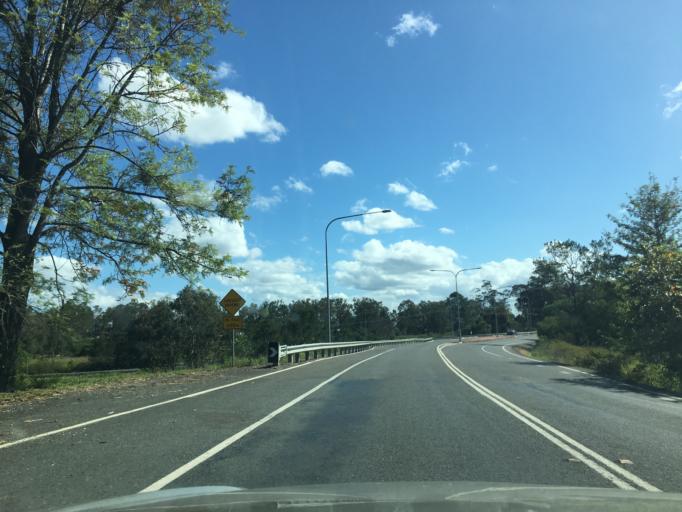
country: AU
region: Queensland
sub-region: Logan
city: Waterford West
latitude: -27.7082
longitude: 153.1464
